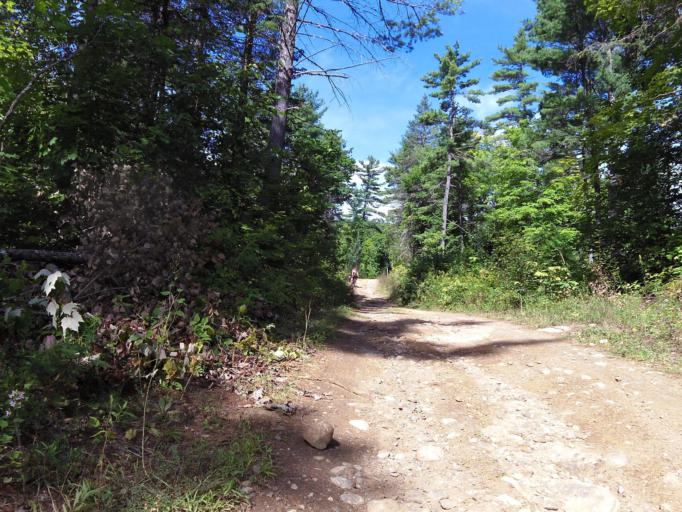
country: CA
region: Ontario
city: Renfrew
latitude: 45.1279
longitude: -76.7274
